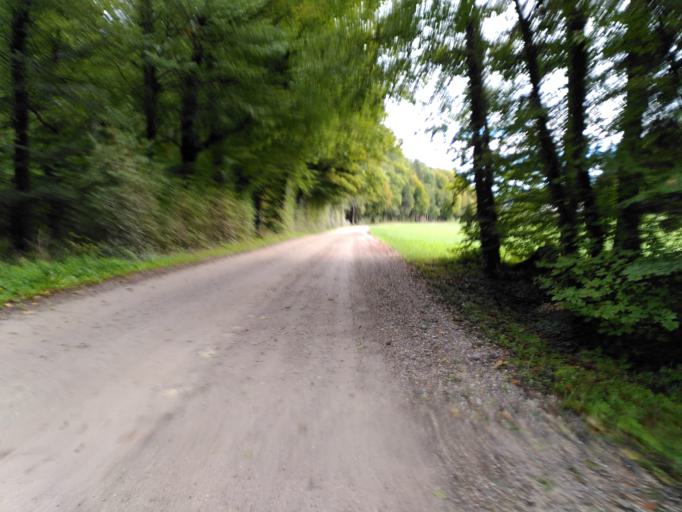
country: CH
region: Bern
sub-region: Emmental District
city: Ersigen
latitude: 47.0974
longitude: 7.6276
